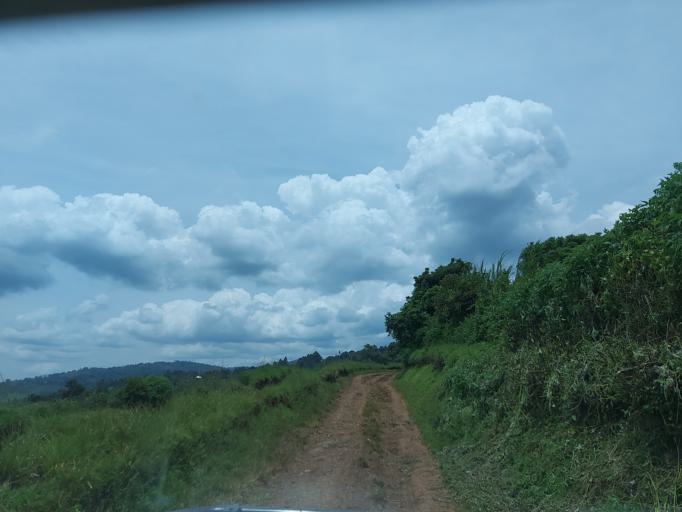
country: CD
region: South Kivu
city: Kabare
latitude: -2.3360
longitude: 28.7832
